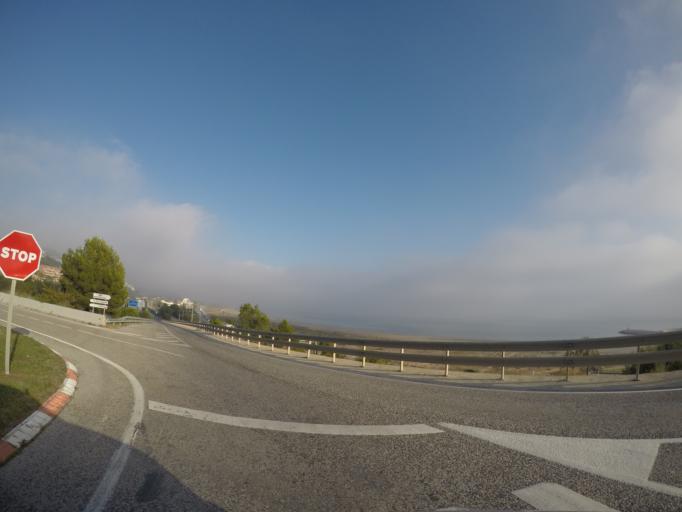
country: ES
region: Catalonia
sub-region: Provincia de Barcelona
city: Castelldefels
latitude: 41.2624
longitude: 1.9279
